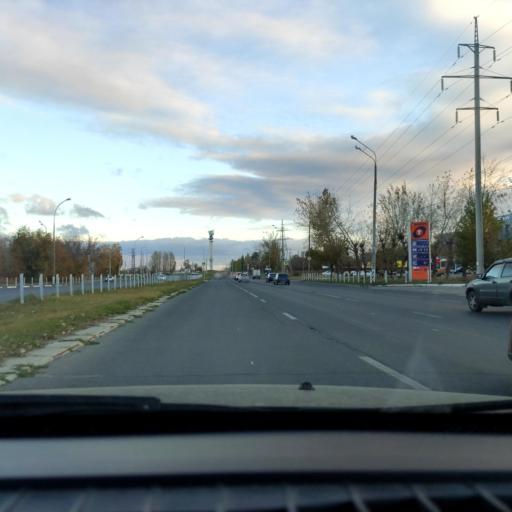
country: RU
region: Samara
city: Tol'yatti
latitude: 53.5500
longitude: 49.2869
